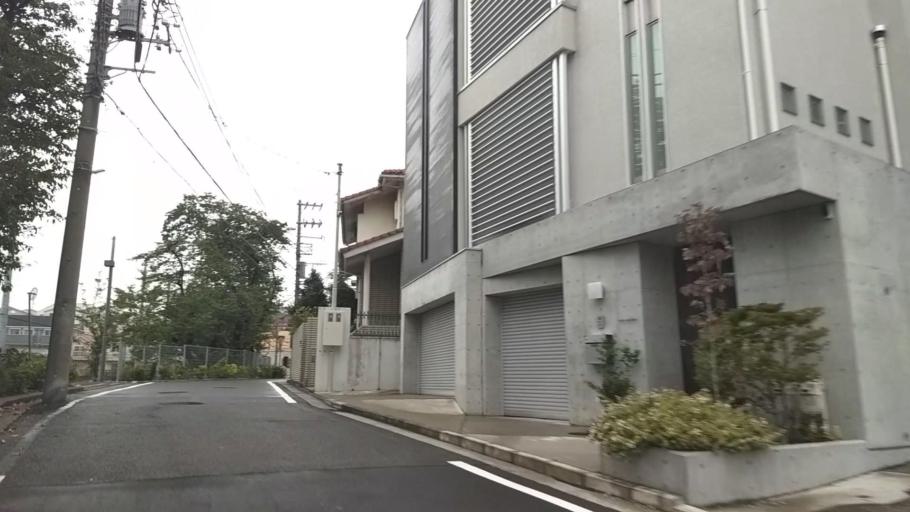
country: JP
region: Kanagawa
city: Yokohama
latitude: 35.4202
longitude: 139.6425
